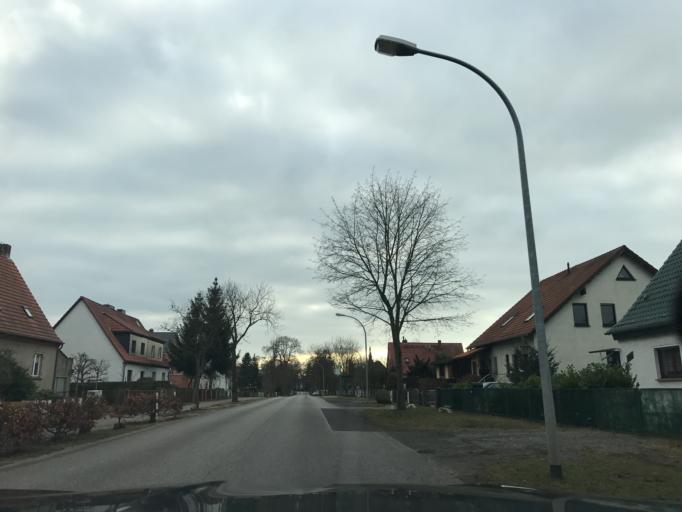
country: DE
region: Brandenburg
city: Brandenburg an der Havel
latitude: 52.3850
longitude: 12.5450
